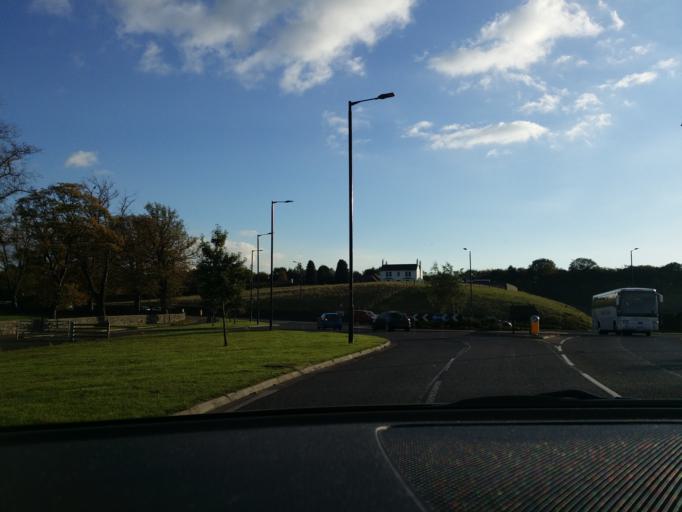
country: GB
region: Scotland
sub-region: Stirling
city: Stirling
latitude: 56.1214
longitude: -3.9519
